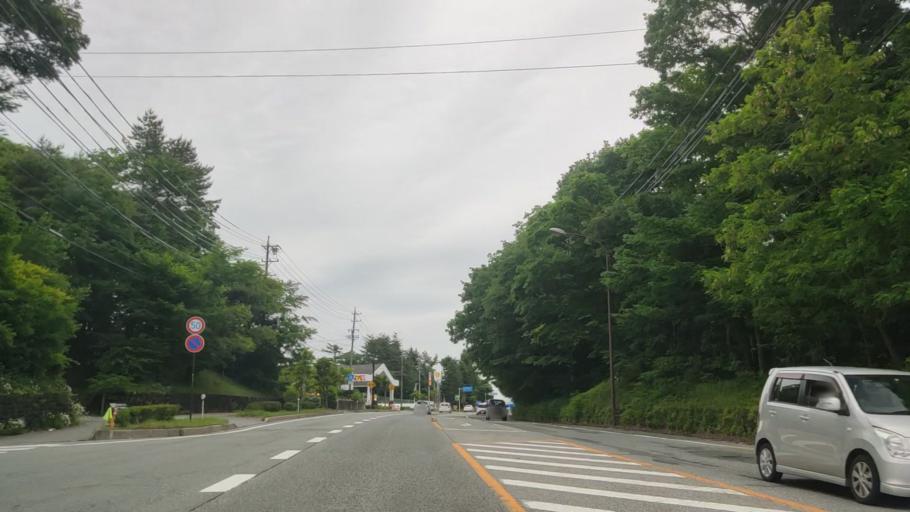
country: JP
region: Nagano
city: Komoro
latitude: 36.3409
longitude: 138.5506
